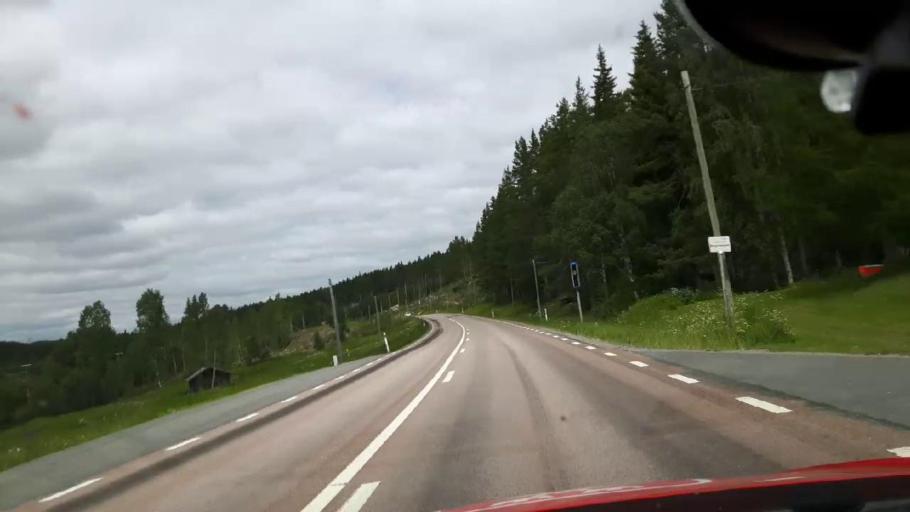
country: SE
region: Jaemtland
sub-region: OEstersunds Kommun
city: Brunflo
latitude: 62.9705
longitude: 15.0196
